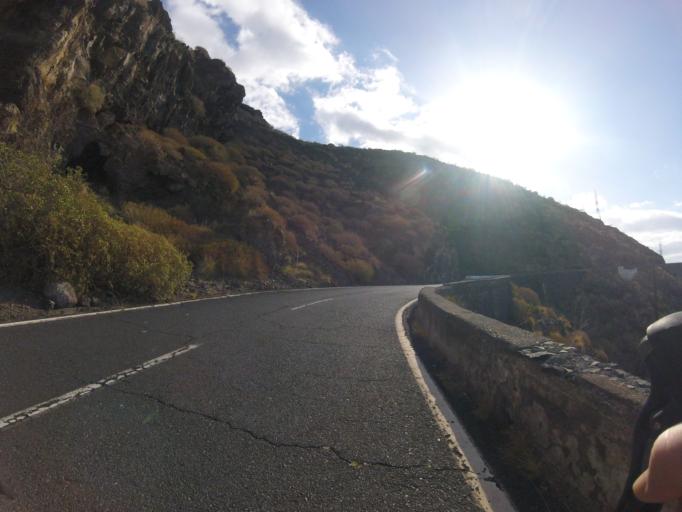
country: ES
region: Canary Islands
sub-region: Provincia de Santa Cruz de Tenerife
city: Candelaria
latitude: 28.3860
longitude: -16.3596
